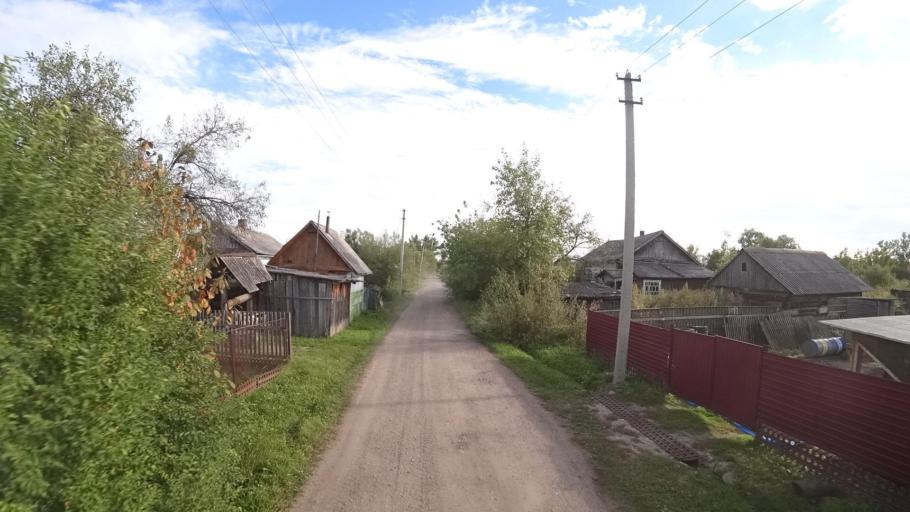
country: RU
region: Primorskiy
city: Dostoyevka
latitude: 44.2908
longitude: 133.4303
